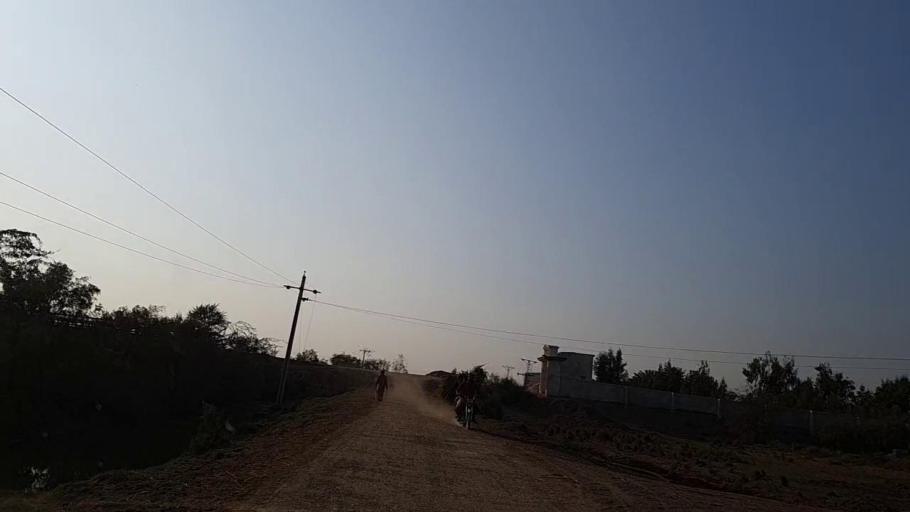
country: PK
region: Sindh
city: Sakrand
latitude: 26.0937
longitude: 68.3962
